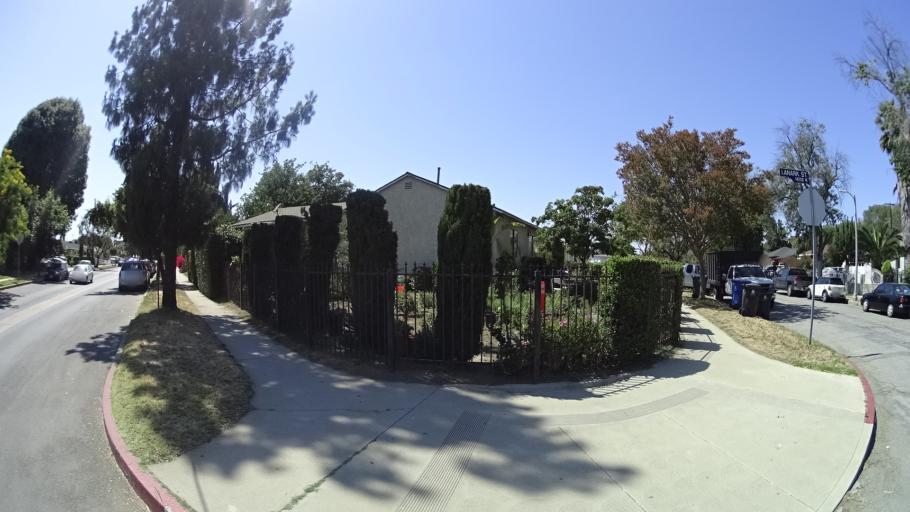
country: US
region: California
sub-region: Los Angeles County
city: Van Nuys
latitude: 34.2175
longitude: -118.4442
